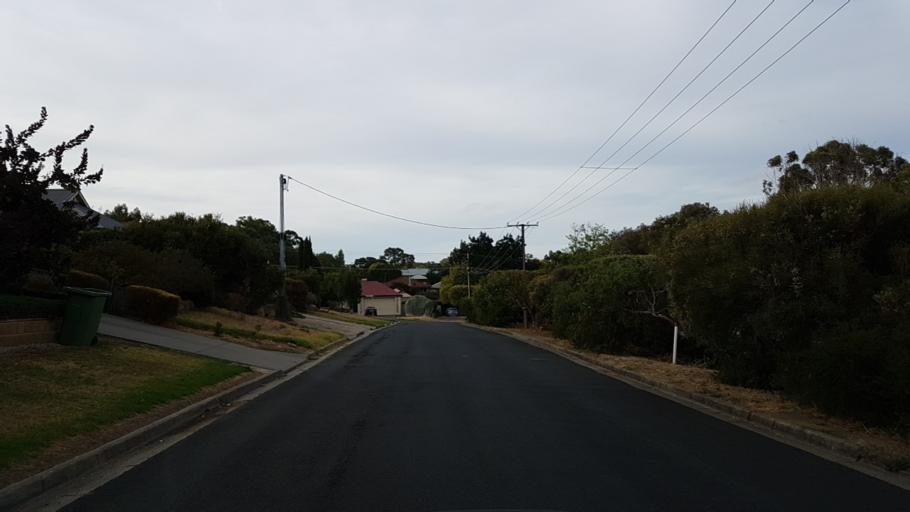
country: AU
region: South Australia
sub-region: Mount Barker
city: Nairne
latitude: -35.0297
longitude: 138.9097
